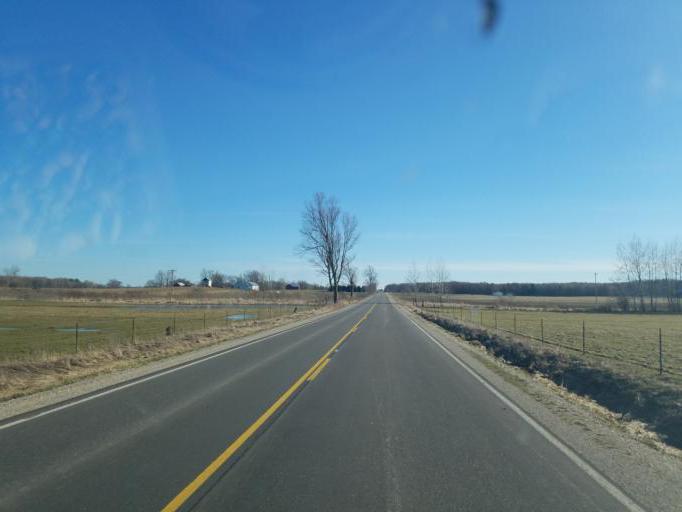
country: US
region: Michigan
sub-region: Montcalm County
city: Lakeview
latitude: 43.5155
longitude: -85.2543
